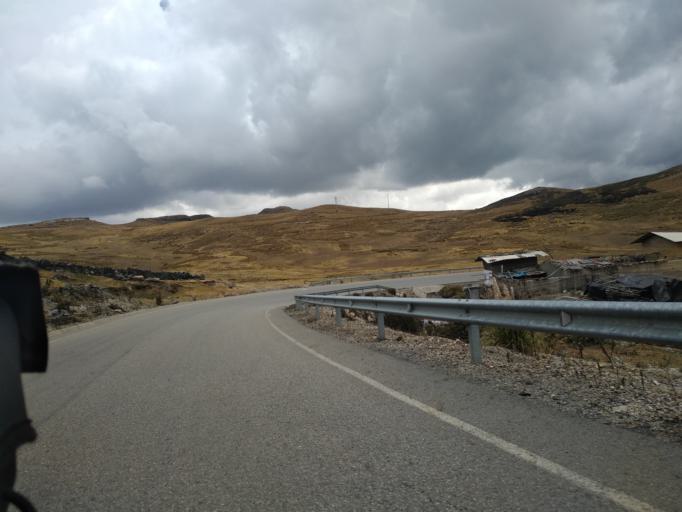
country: PE
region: La Libertad
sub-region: Provincia de Santiago de Chuco
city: Quiruvilca
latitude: -7.9896
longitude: -78.2777
